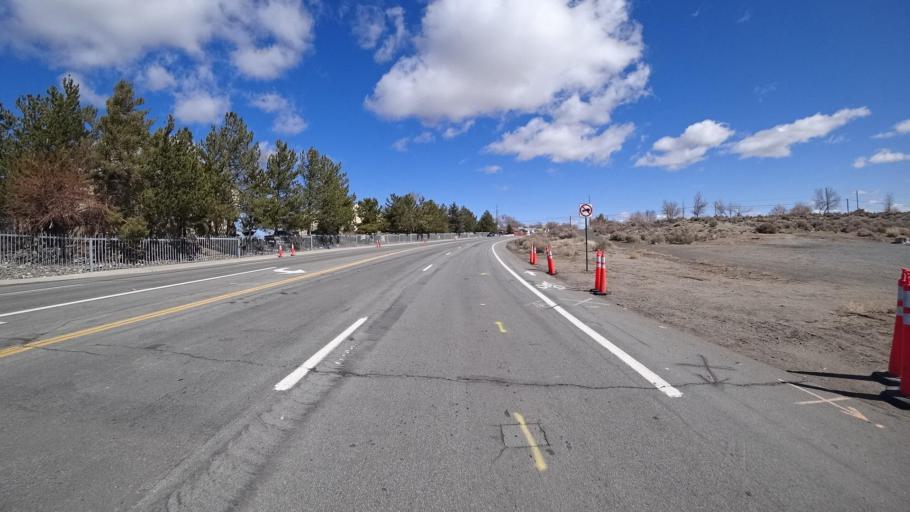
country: US
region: Nevada
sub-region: Washoe County
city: Lemmon Valley
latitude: 39.6447
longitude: -119.8812
